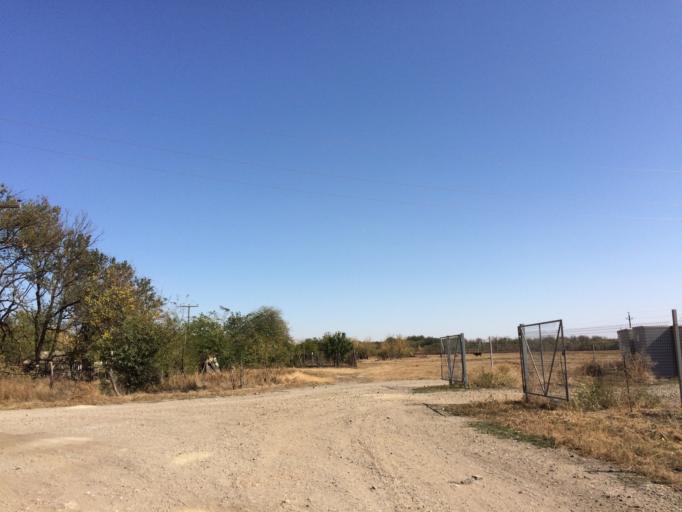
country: RU
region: Rostov
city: Tselina
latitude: 46.5136
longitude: 41.1825
